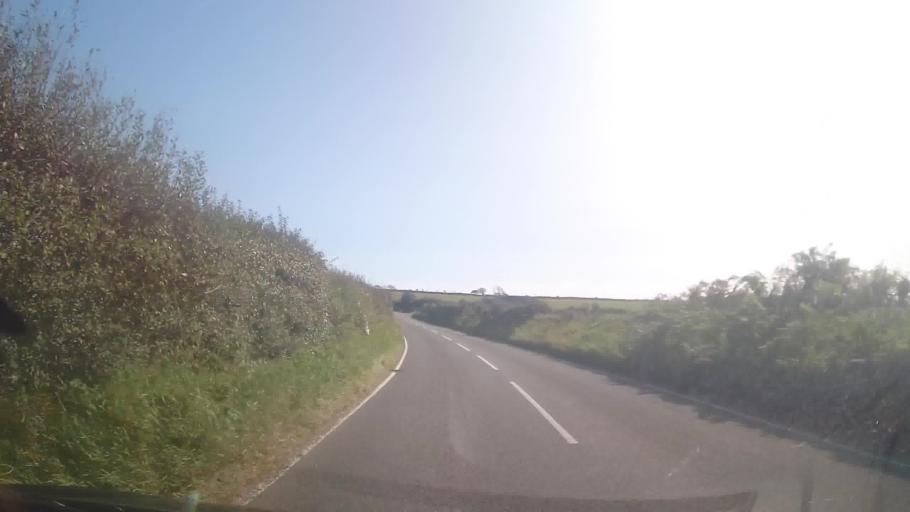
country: GB
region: Wales
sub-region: Pembrokeshire
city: Scleddau
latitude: 51.9341
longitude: -5.0127
